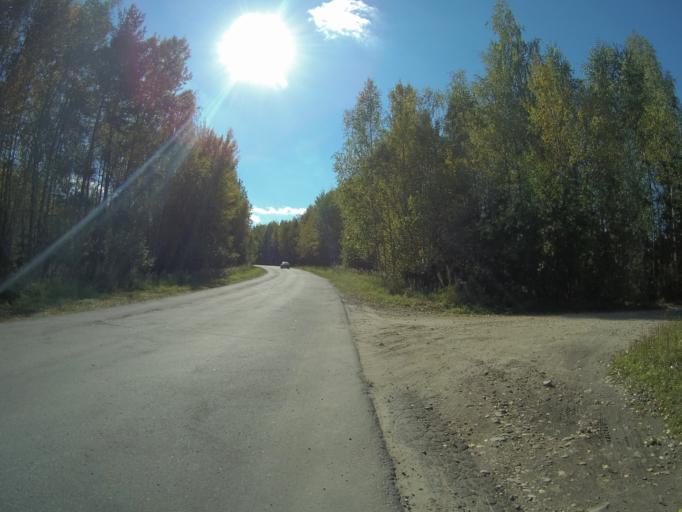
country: RU
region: Vladimir
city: Raduzhnyy
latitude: 55.9682
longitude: 40.2442
